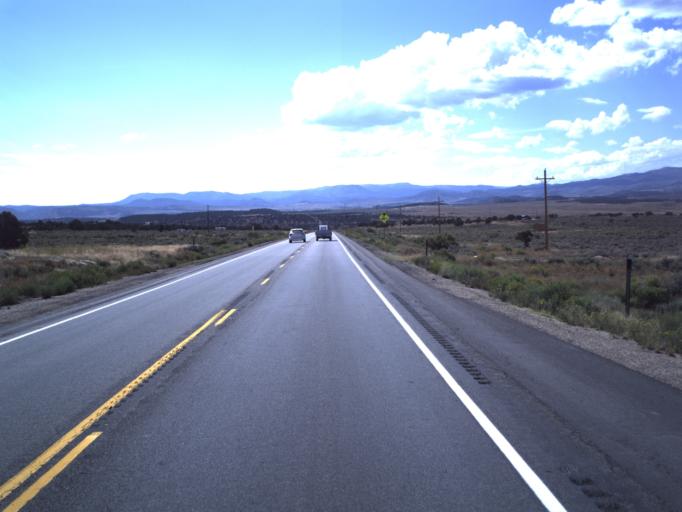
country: US
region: Utah
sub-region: Duchesne County
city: Duchesne
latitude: 40.2075
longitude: -110.7379
